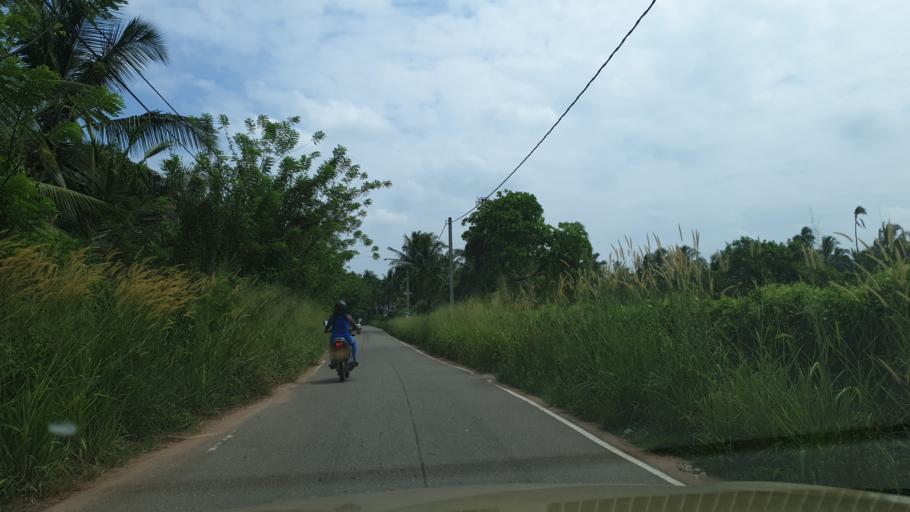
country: LK
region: North Western
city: Kuliyapitiya
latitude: 7.3538
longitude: 79.9677
